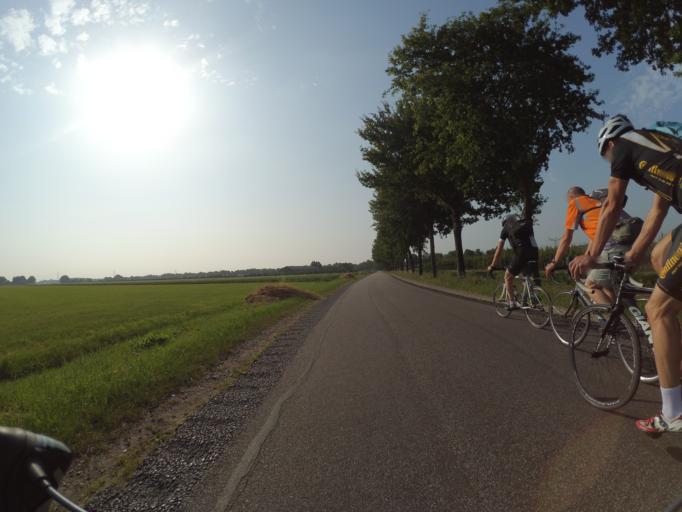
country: NL
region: North Brabant
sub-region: Gemeente Dongen
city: Dongen
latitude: 51.6320
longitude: 4.9689
